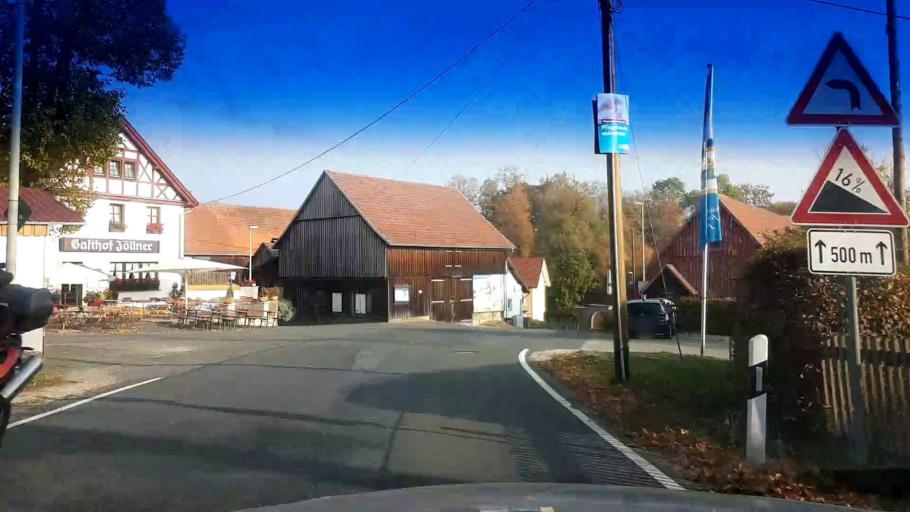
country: DE
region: Bavaria
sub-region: Upper Franconia
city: Stadelhofen
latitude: 50.0188
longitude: 11.2017
